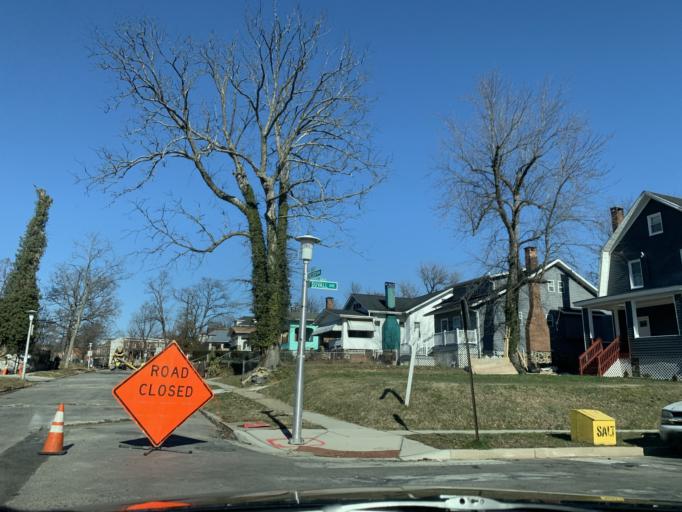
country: US
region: Maryland
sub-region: Baltimore County
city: Lochearn
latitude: 39.3200
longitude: -76.6819
